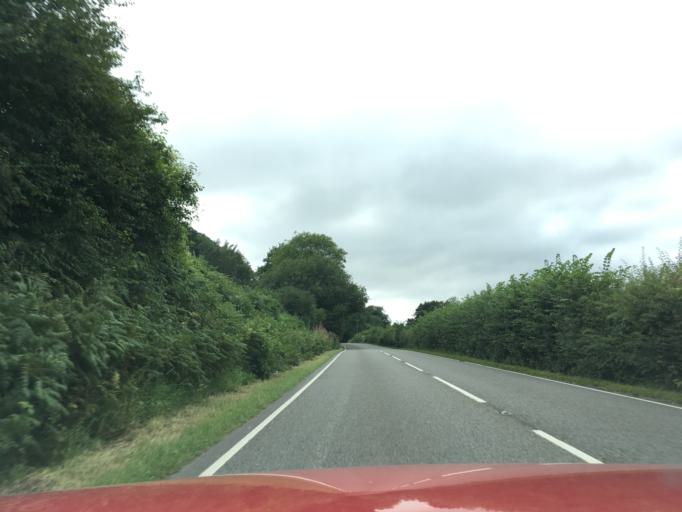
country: GB
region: England
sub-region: Hampshire
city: Petersfield
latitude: 51.0090
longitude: -0.9819
